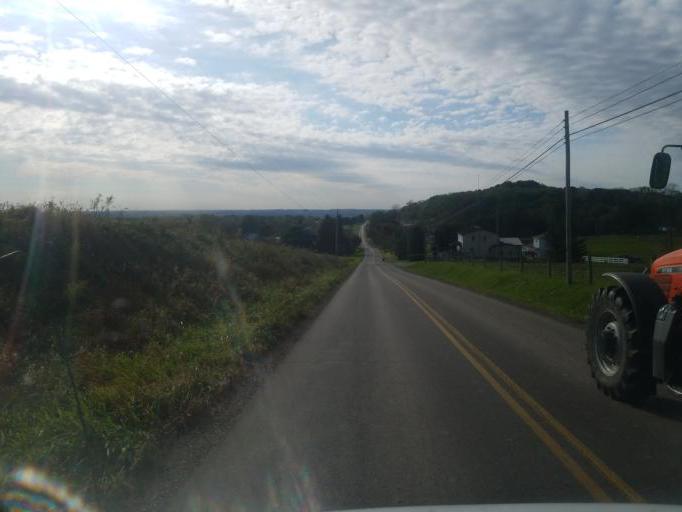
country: US
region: Ohio
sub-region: Wayne County
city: Apple Creek
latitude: 40.6736
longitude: -81.9039
